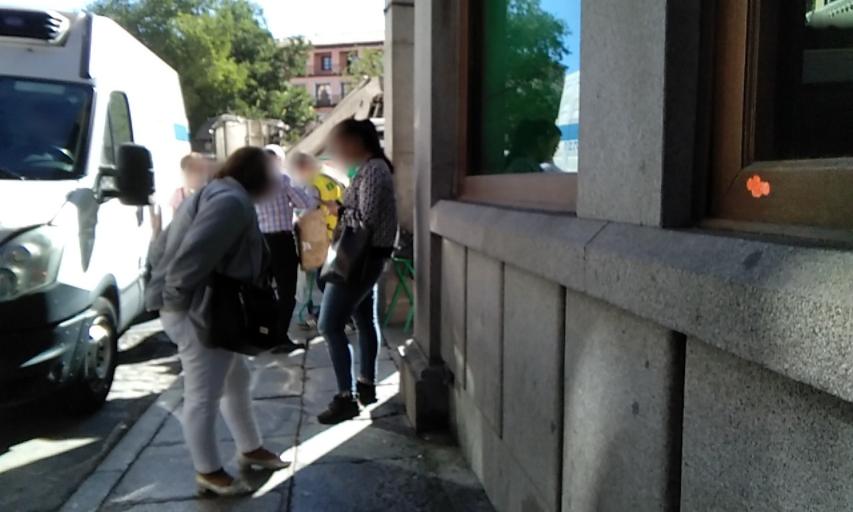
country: ES
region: Castille-La Mancha
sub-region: Province of Toledo
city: Toledo
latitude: 39.8594
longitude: -4.0221
